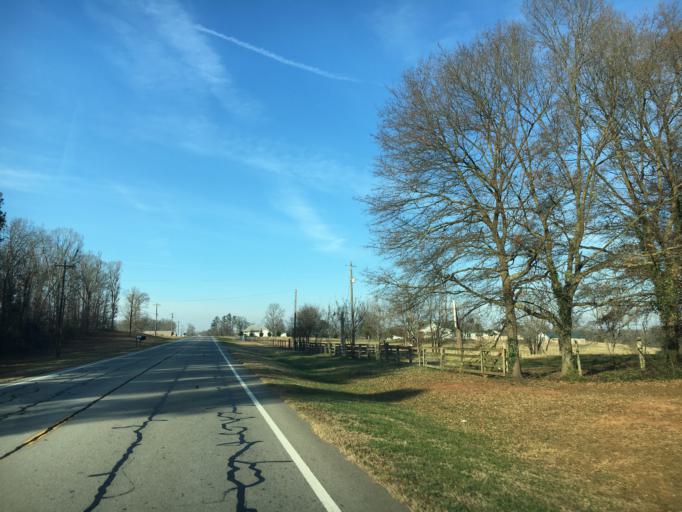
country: US
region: Georgia
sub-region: Franklin County
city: Lavonia
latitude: 34.4166
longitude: -83.0260
